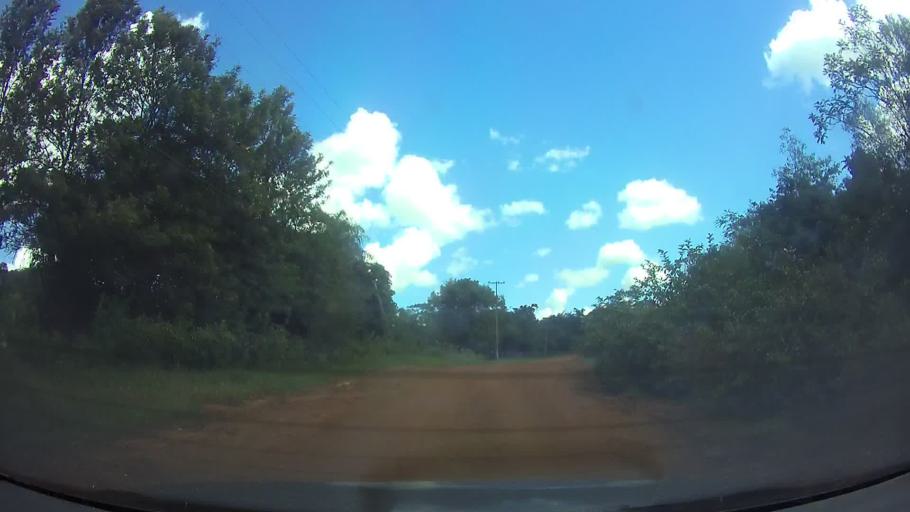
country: PY
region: Paraguari
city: La Colmena
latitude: -25.9321
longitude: -56.7838
